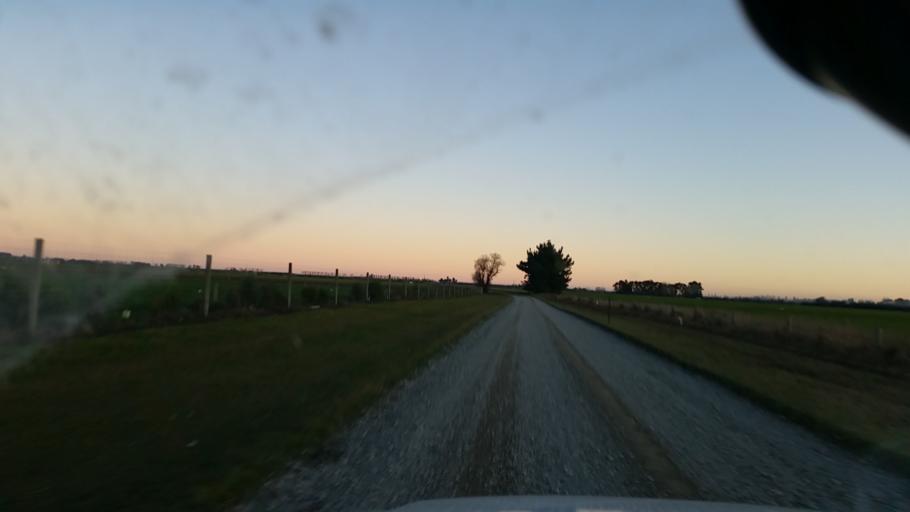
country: NZ
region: Canterbury
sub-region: Ashburton District
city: Tinwald
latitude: -44.0598
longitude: 171.6610
